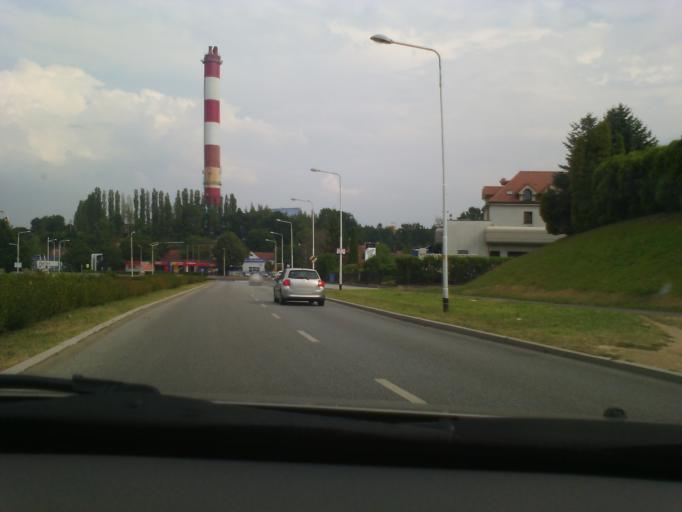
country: PL
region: Lower Silesian Voivodeship
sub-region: Powiat walbrzyski
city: Szczawno-Zdroj
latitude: 50.8193
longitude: 16.2764
